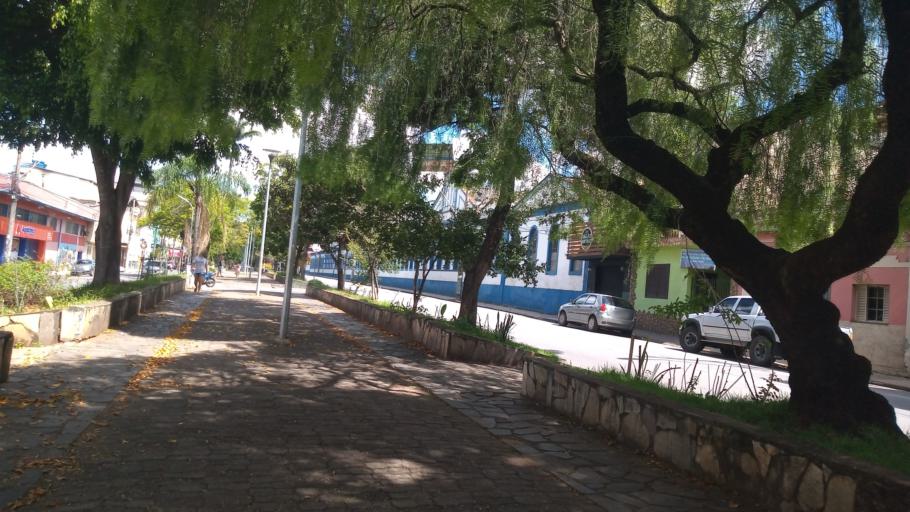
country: BR
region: Minas Gerais
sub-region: Sao Joao Del Rei
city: Sao Joao del Rei
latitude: -21.1259
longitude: -44.2487
